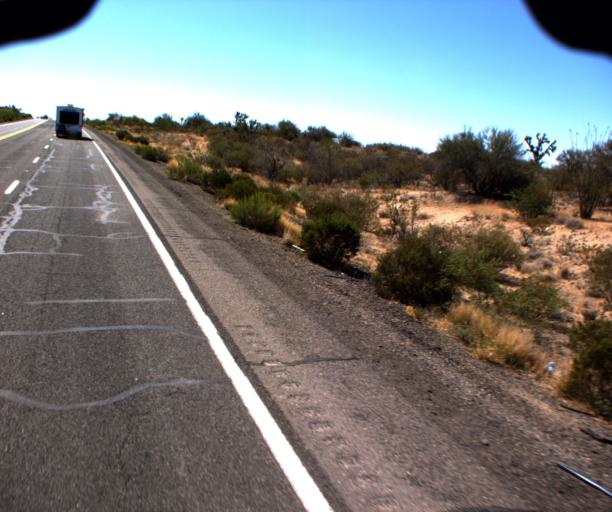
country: US
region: Arizona
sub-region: Yavapai County
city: Congress
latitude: 34.1900
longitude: -113.0521
